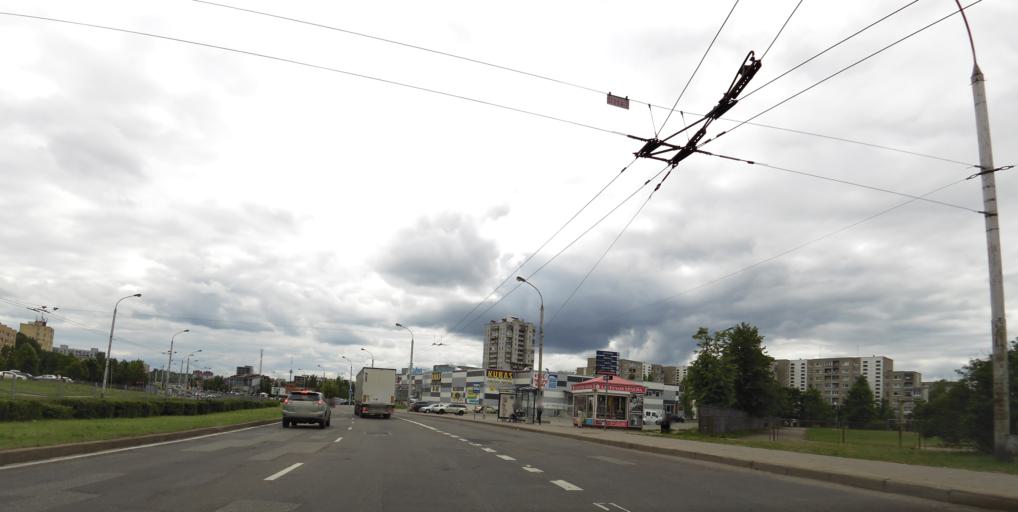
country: LT
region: Vilnius County
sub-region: Vilnius
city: Fabijoniskes
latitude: 54.7281
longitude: 25.2342
